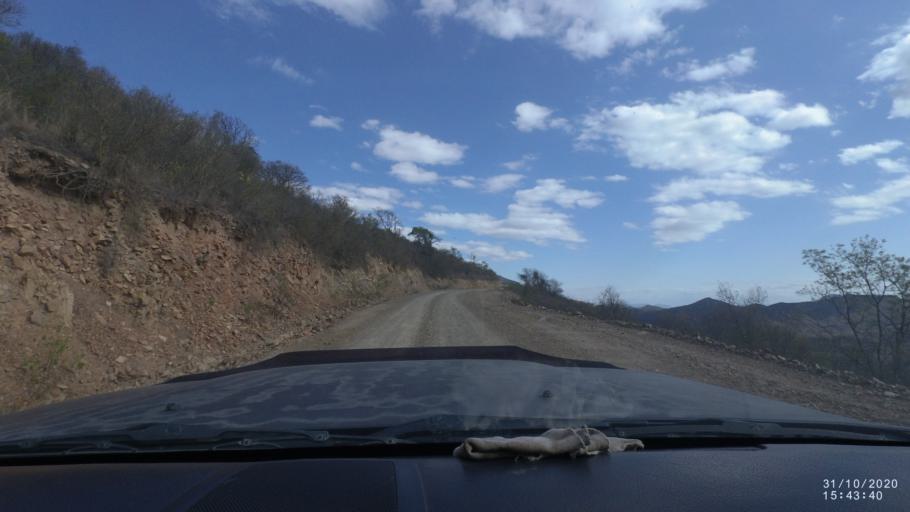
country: BO
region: Chuquisaca
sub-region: Provincia Zudanez
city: Mojocoya
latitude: -18.3185
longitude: -64.7269
